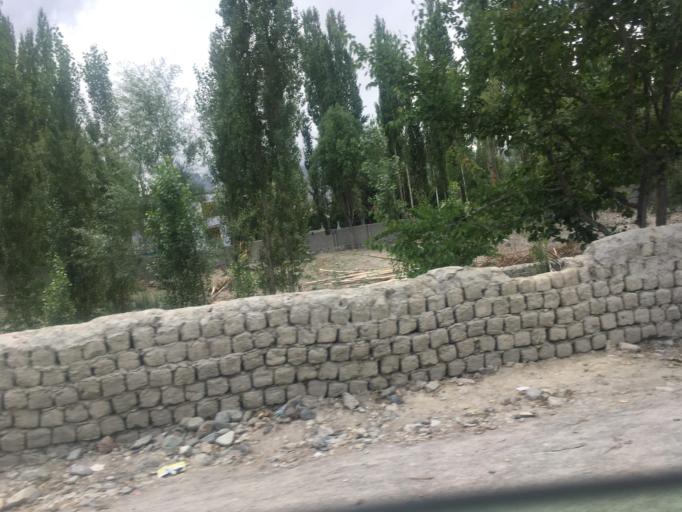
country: PK
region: Gilgit-Baltistan
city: Skardu
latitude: 35.2930
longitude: 75.6124
